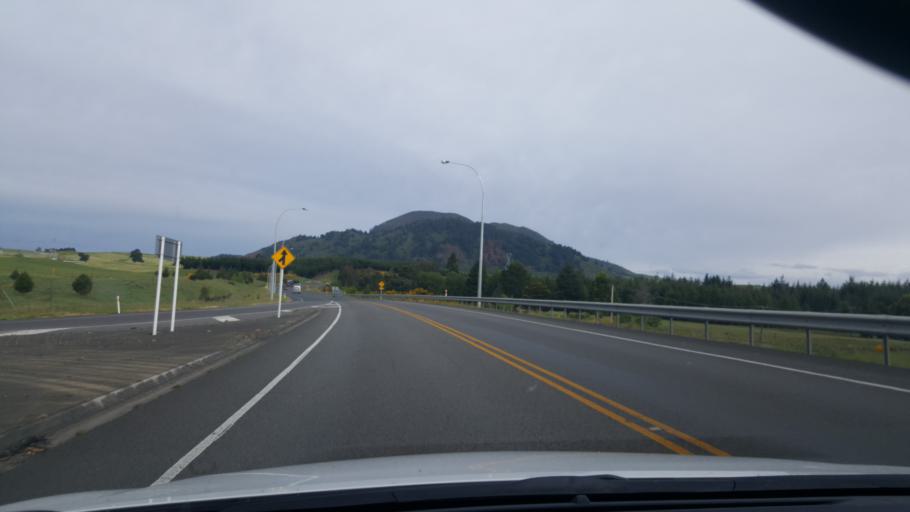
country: NZ
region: Waikato
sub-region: Taupo District
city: Taupo
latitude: -38.6693
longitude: 176.1057
